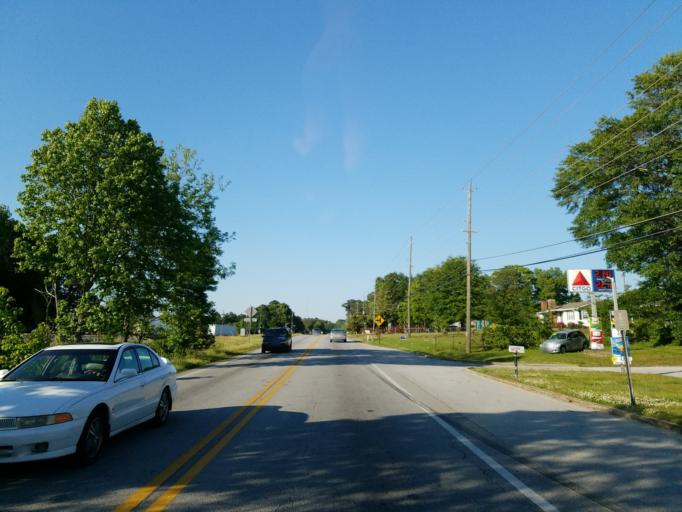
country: US
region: Georgia
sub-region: Douglas County
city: Douglasville
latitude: 33.7671
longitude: -84.7167
